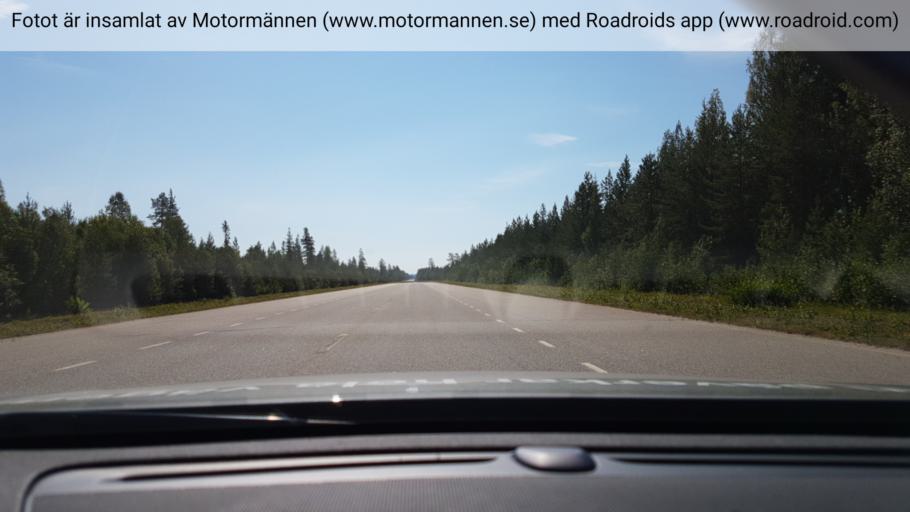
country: SE
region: Vaesterbotten
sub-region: Norsjo Kommun
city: Norsjoe
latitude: 64.5711
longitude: 19.3105
